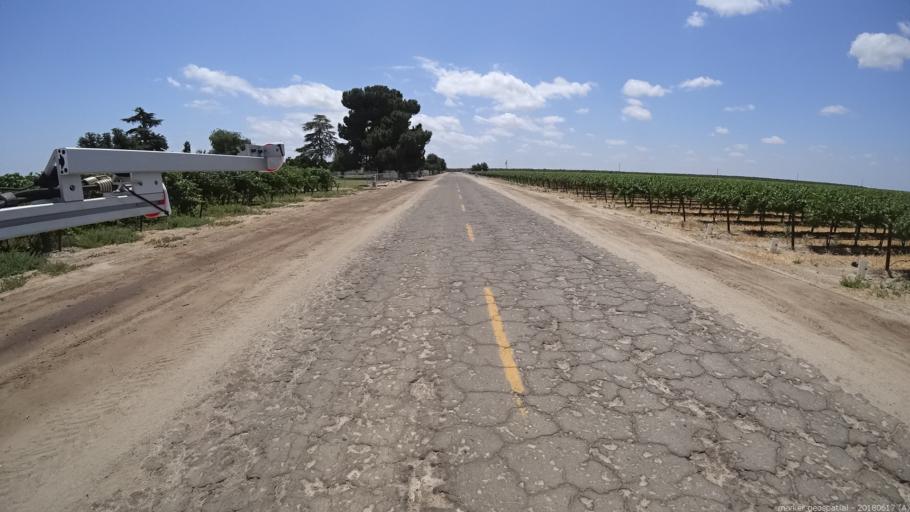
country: US
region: California
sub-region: Fresno County
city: Kerman
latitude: 36.8321
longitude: -120.2113
